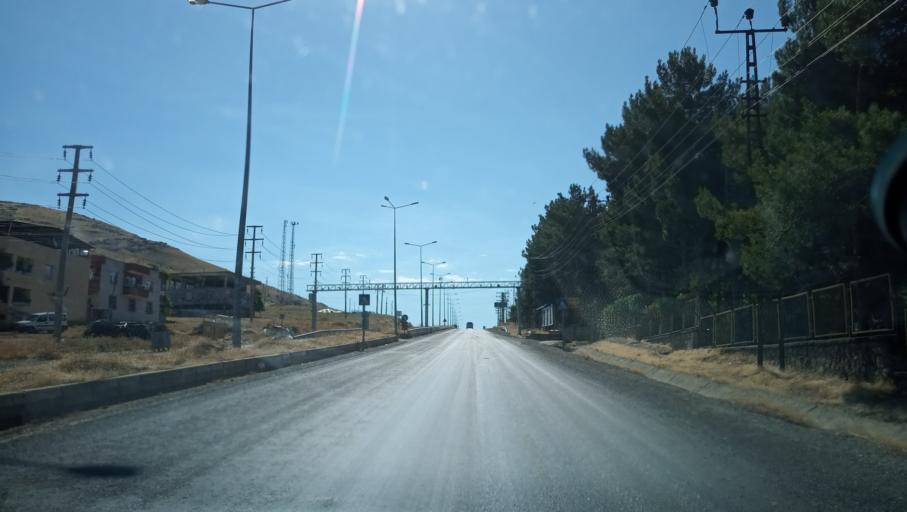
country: TR
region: Diyarbakir
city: Silvan
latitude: 38.1339
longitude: 41.0384
